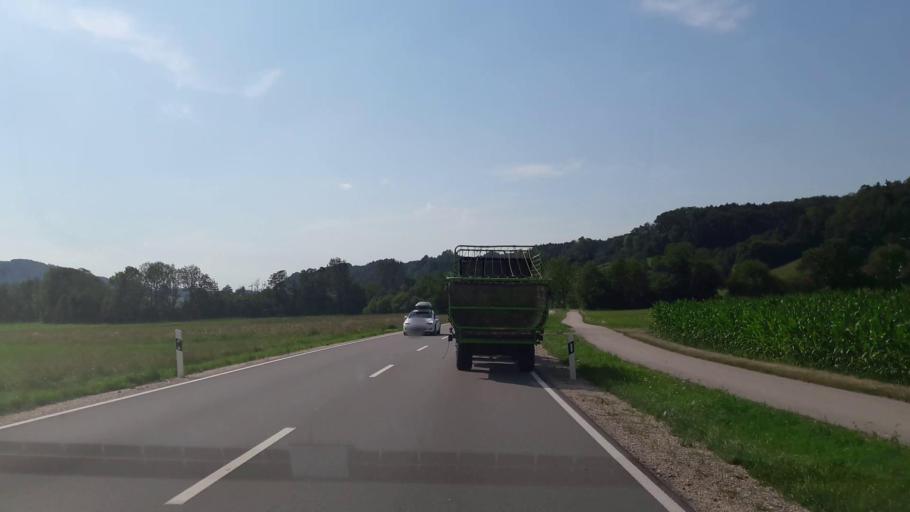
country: DE
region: Bavaria
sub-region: Upper Bavaria
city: Teisendorf
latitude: 47.8553
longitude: 12.7780
